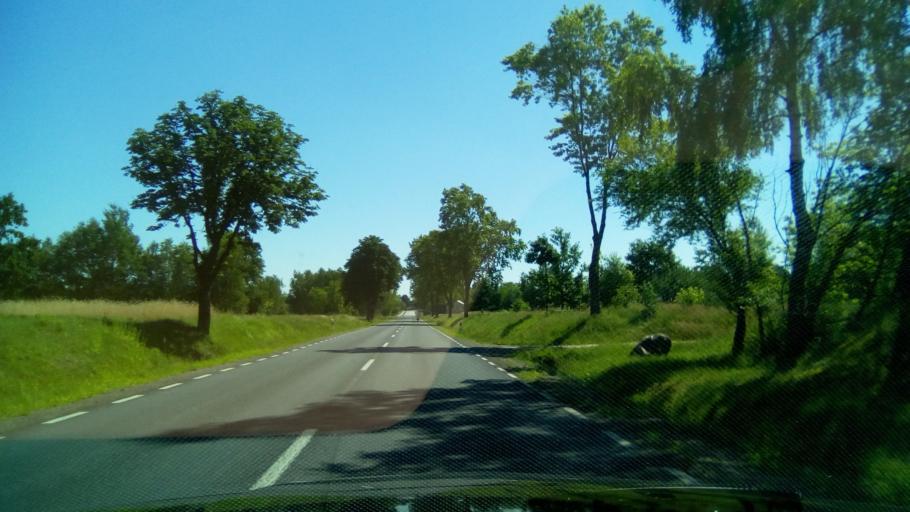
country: PL
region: Masovian Voivodeship
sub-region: Powiat przysuski
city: Odrzywol
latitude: 51.5198
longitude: 20.5069
